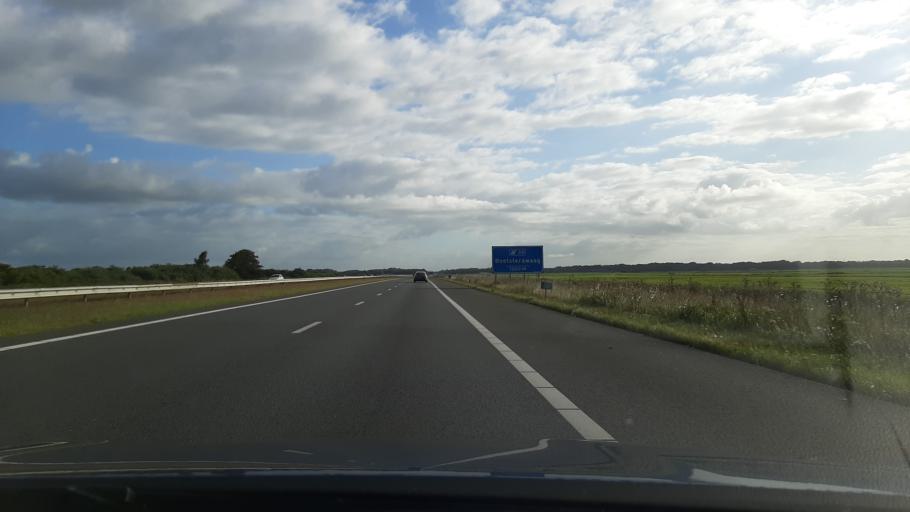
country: NL
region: Friesland
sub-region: Gemeente Smallingerland
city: Boornbergum
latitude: 53.0479
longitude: 6.0378
